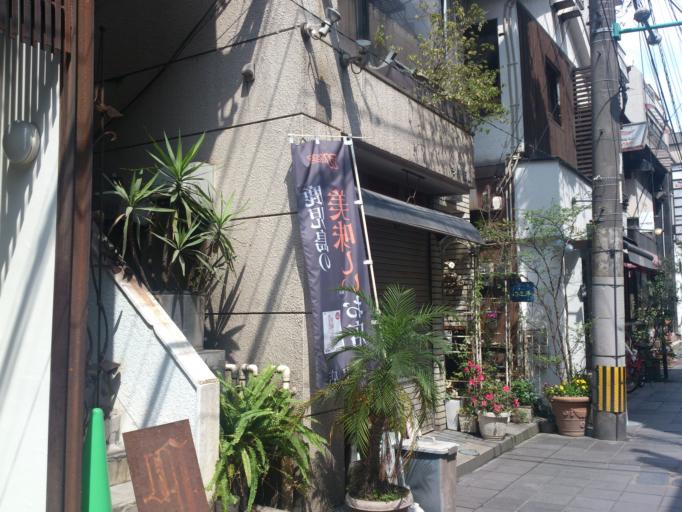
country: JP
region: Kagoshima
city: Kagoshima-shi
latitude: 31.5917
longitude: 130.5535
